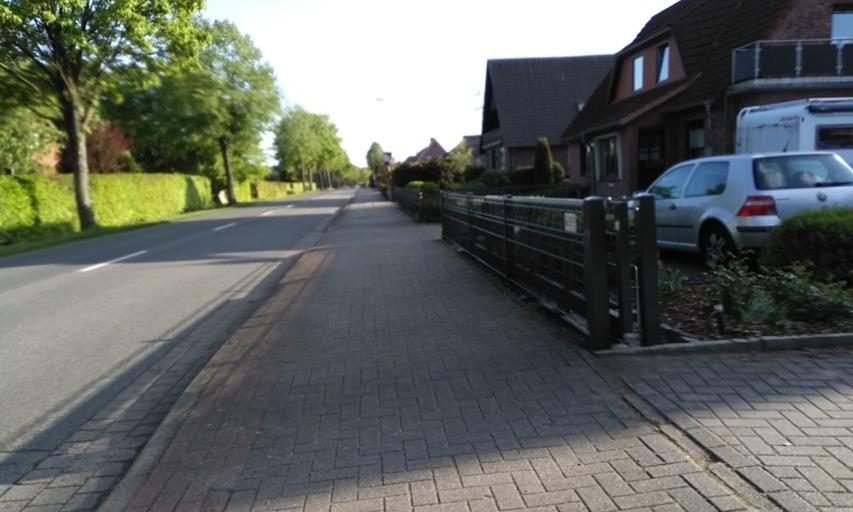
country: DE
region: Lower Saxony
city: Wohnste
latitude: 53.4065
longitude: 9.5444
